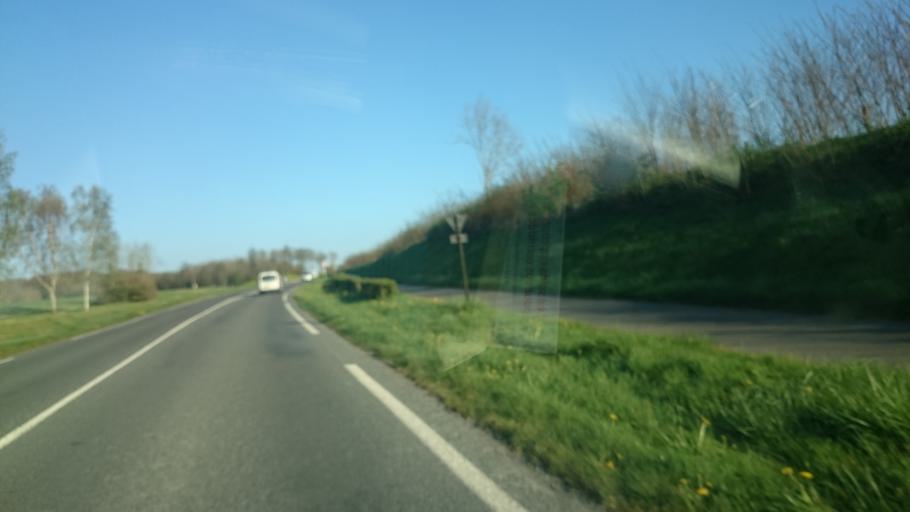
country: FR
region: Picardie
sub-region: Departement de la Somme
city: Pende
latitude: 50.1834
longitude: 1.5922
